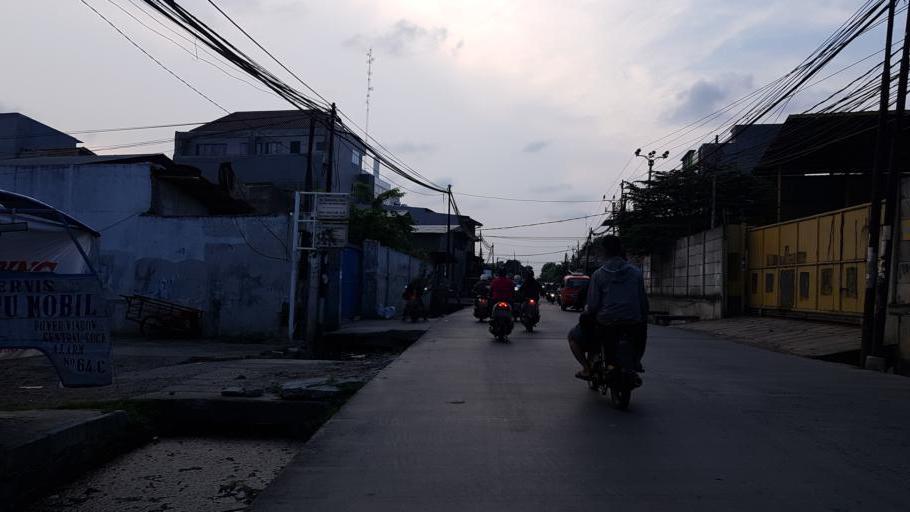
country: ID
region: Jakarta Raya
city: Jakarta
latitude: -6.1409
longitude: 106.7688
